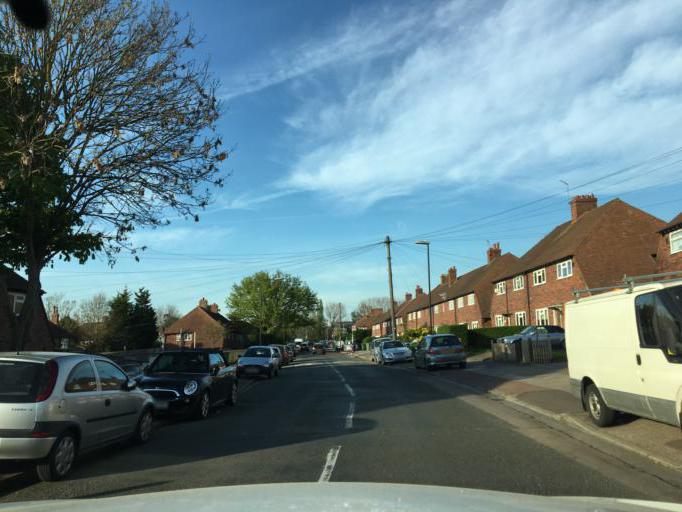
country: GB
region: England
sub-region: Greater London
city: Chislehurst
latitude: 51.4469
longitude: 0.0433
